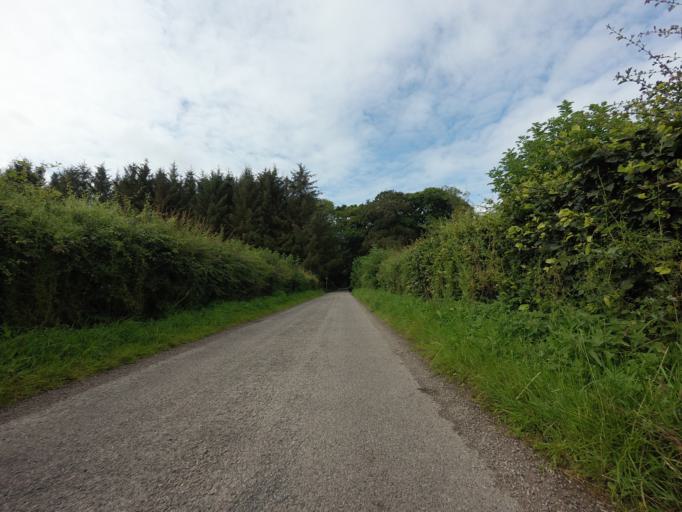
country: GB
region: Scotland
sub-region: Moray
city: Hopeman
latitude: 57.6724
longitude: -3.4107
